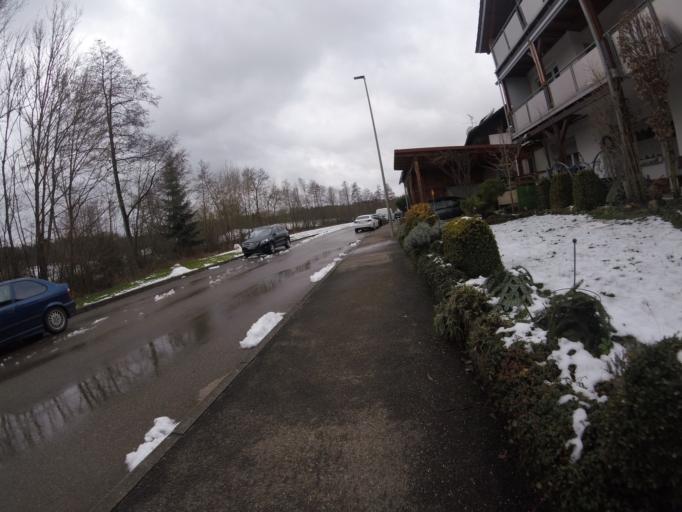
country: DE
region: Baden-Wuerttemberg
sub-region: Regierungsbezirk Stuttgart
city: Oberstenfeld
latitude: 48.9922
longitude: 9.3549
